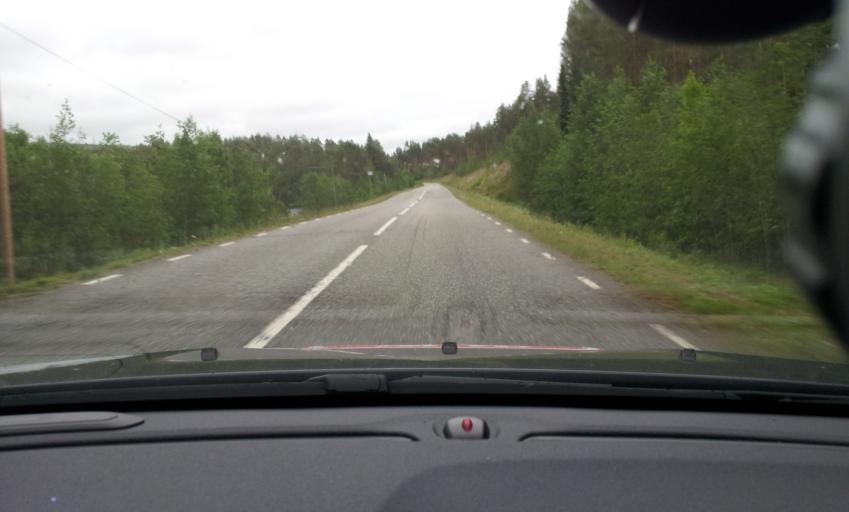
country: SE
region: Jaemtland
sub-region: Ragunda Kommun
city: Hammarstrand
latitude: 63.2606
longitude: 15.8923
